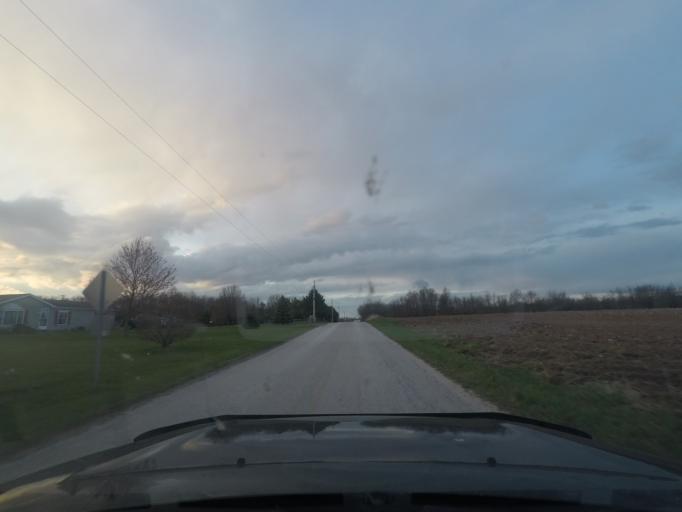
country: US
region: Indiana
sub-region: LaPorte County
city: Kingsford Heights
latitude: 41.4676
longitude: -86.6999
